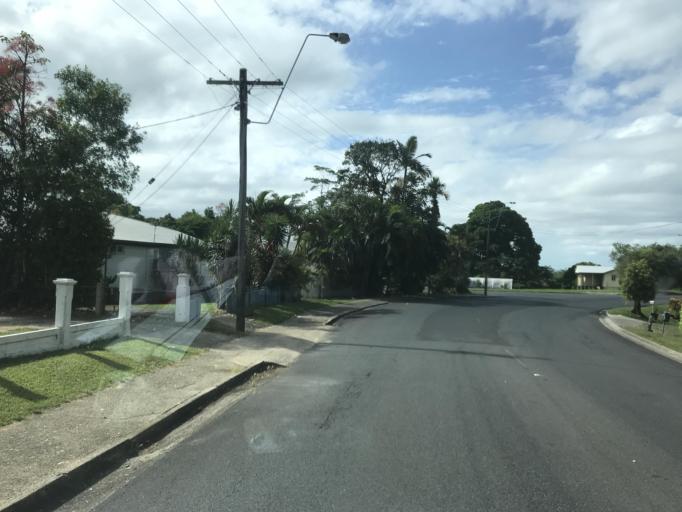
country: AU
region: Queensland
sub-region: Cassowary Coast
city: Innisfail
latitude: -17.5300
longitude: 146.0347
